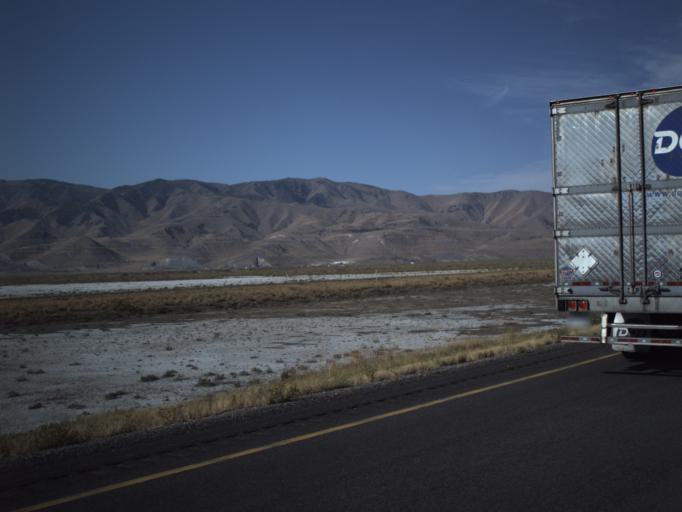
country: US
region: Utah
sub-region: Tooele County
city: Grantsville
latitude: 40.7024
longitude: -112.4953
